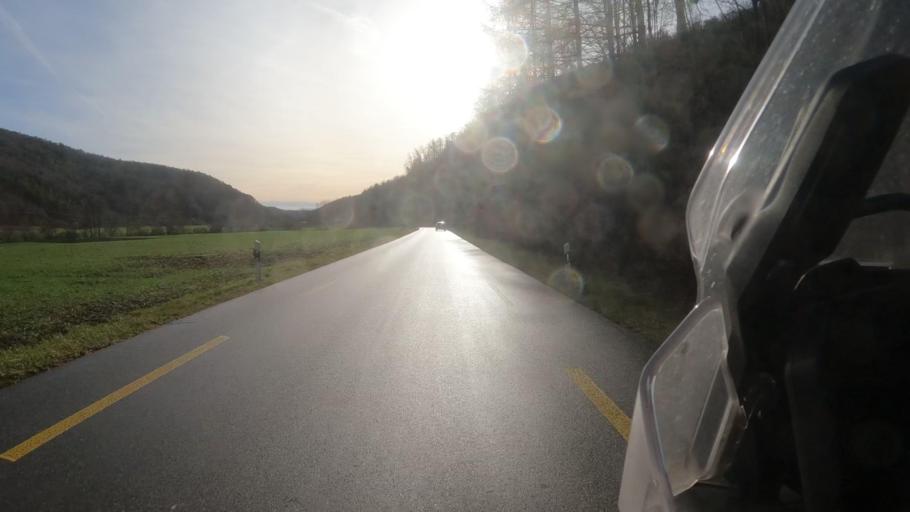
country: CH
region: Schaffhausen
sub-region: Bezirk Reiat
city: Stetten
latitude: 47.7409
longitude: 8.6182
